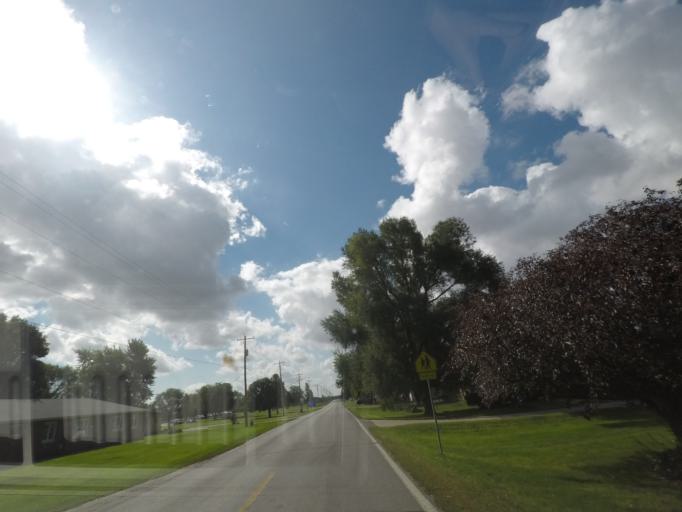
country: US
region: Iowa
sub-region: Story County
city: Nevada
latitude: 42.0124
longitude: -93.3192
